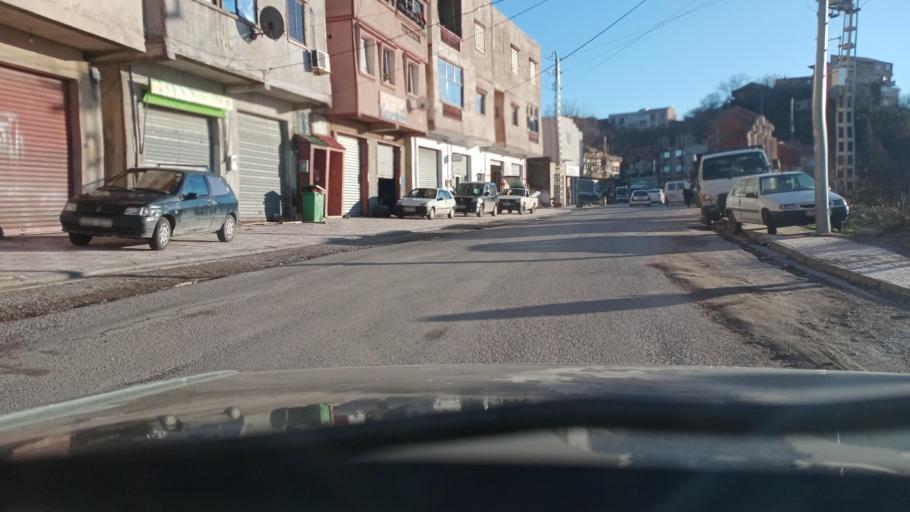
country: DZ
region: Tizi Ouzou
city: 'Ain el Hammam
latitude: 36.5618
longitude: 4.3242
